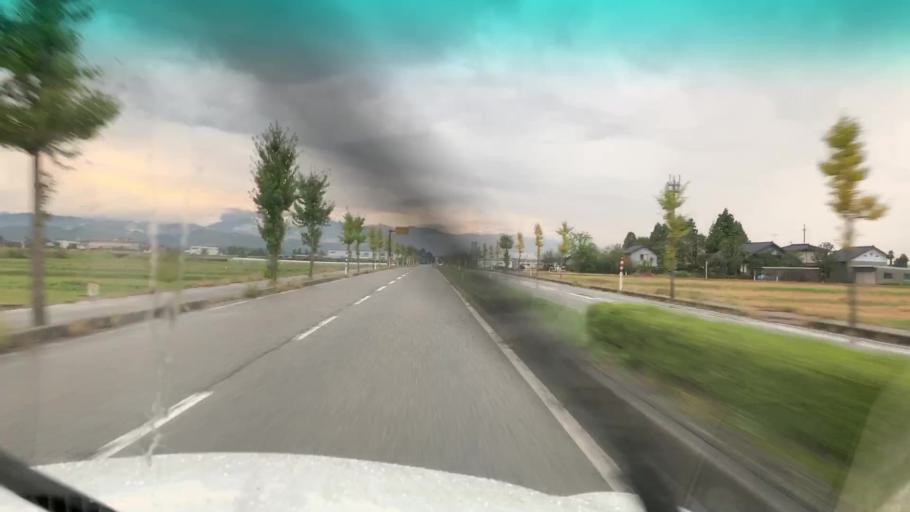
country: JP
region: Toyama
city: Kamiichi
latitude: 36.6759
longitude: 137.3273
